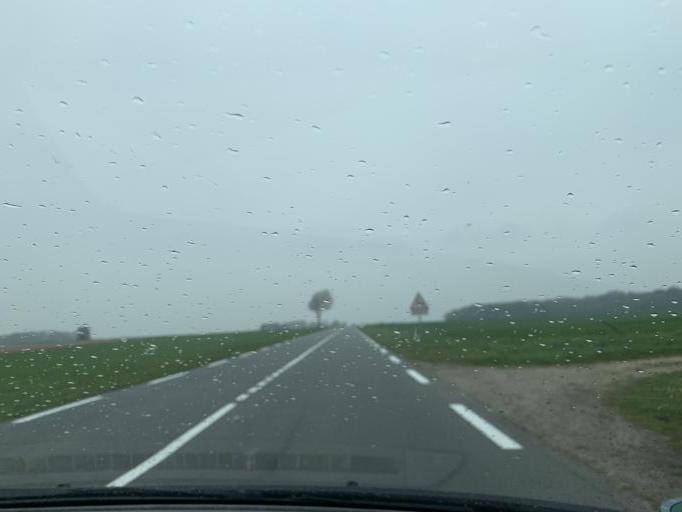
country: FR
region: Picardie
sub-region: Departement de la Somme
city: Nouvion
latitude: 50.1921
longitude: 1.7926
